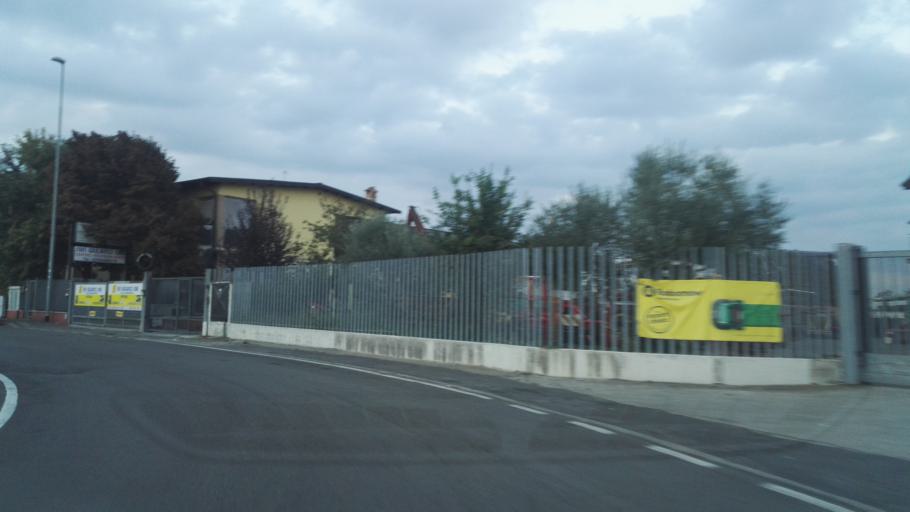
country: IT
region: Lombardy
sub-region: Citta metropolitana di Milano
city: Colturano
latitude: 45.3803
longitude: 9.3098
